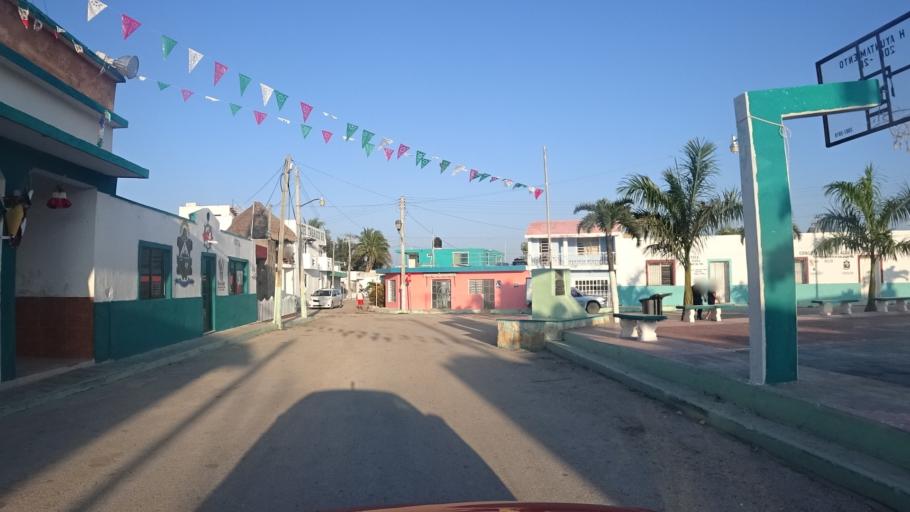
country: MX
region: Yucatan
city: Rio Lagartos
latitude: 21.5978
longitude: -88.1580
